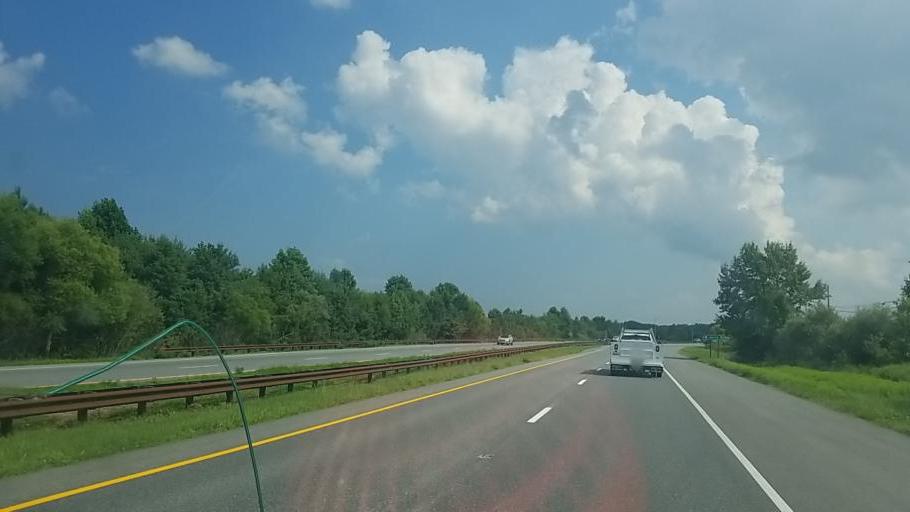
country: US
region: Delaware
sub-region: Sussex County
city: Selbyville
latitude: 38.4182
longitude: -75.2139
